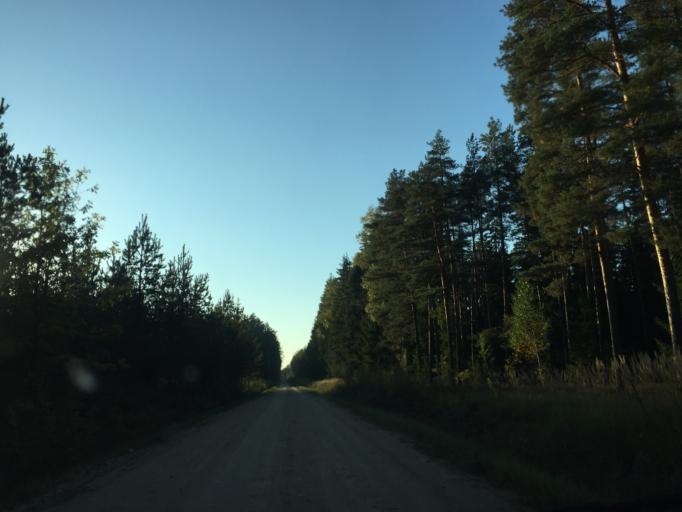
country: LV
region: Seja
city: Loja
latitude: 57.1269
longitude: 24.6281
